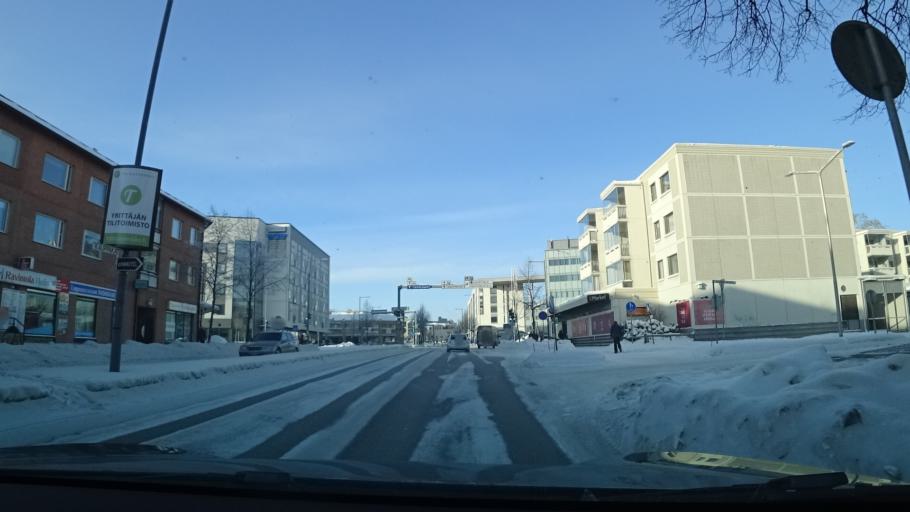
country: FI
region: South Karelia
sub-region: Lappeenranta
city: Lappeenranta
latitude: 61.0539
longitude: 28.1910
